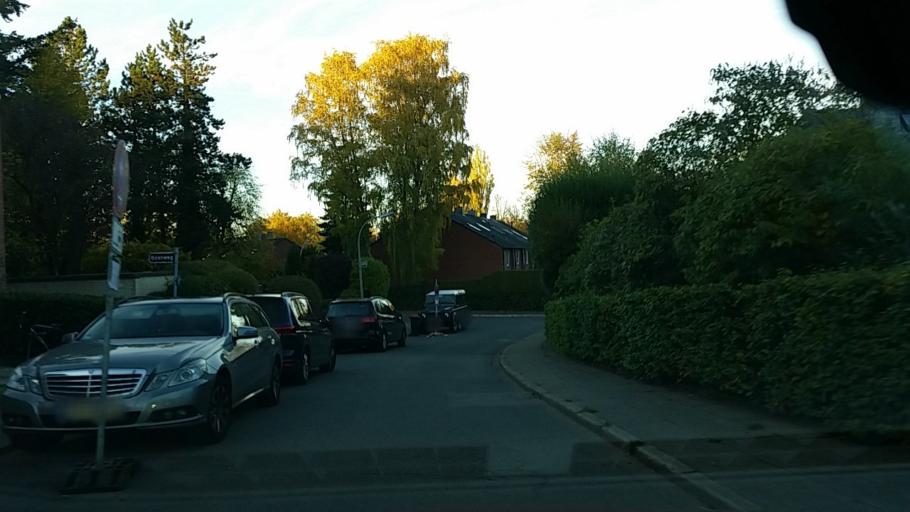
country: DE
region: Schleswig-Holstein
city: Rellingen
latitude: 53.5684
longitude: 9.7888
